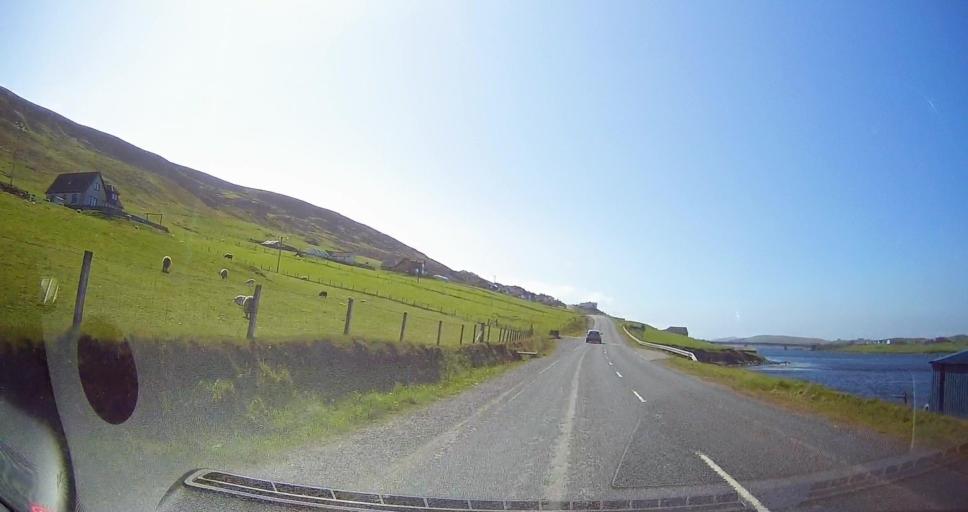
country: GB
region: Scotland
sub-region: Shetland Islands
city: Lerwick
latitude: 60.1359
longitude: -1.2667
